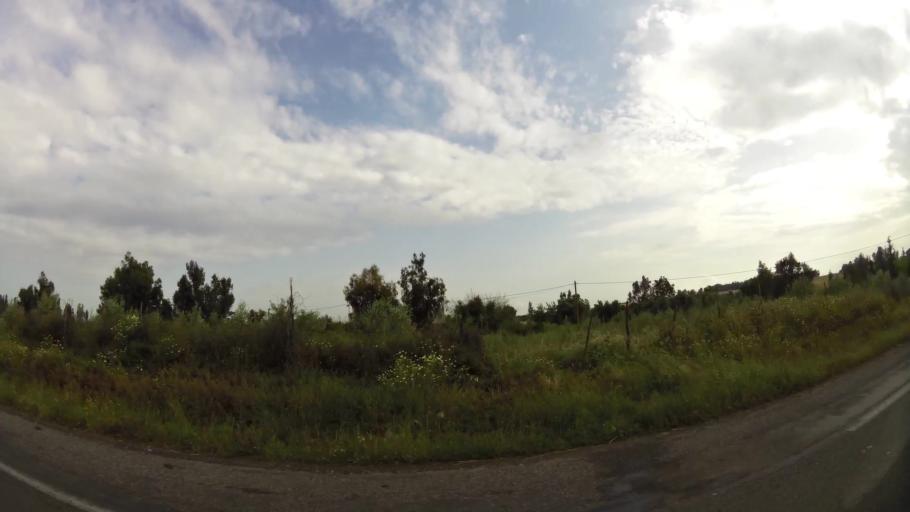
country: MA
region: Rabat-Sale-Zemmour-Zaer
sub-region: Khemisset
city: Khemisset
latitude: 33.7936
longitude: -6.1071
